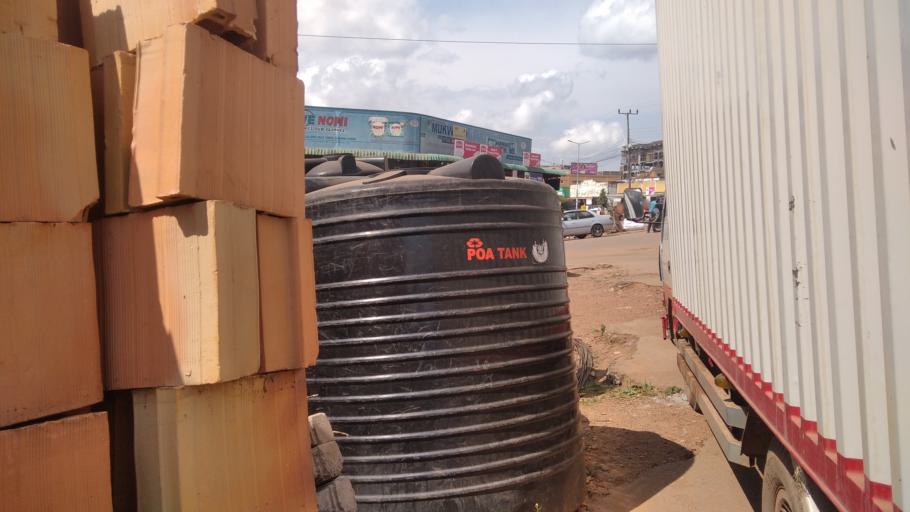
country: UG
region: Central Region
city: Masaka
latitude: -0.3416
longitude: 31.7386
